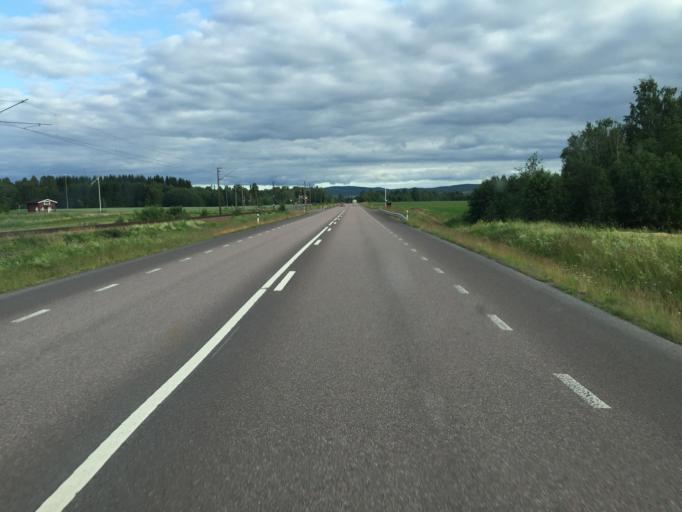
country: SE
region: Dalarna
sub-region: Gagnefs Kommun
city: Djuras
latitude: 60.5761
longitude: 15.1227
